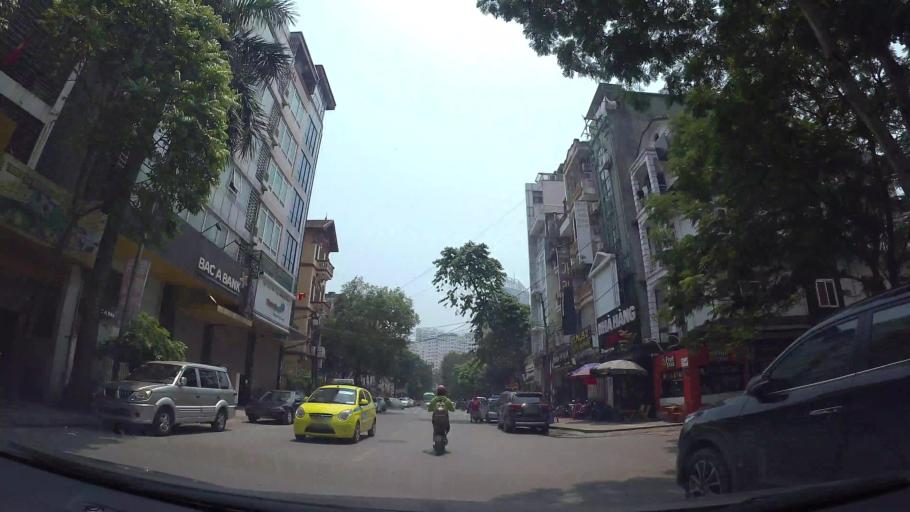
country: VN
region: Ha Noi
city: Thanh Xuan
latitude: 21.0105
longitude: 105.8046
